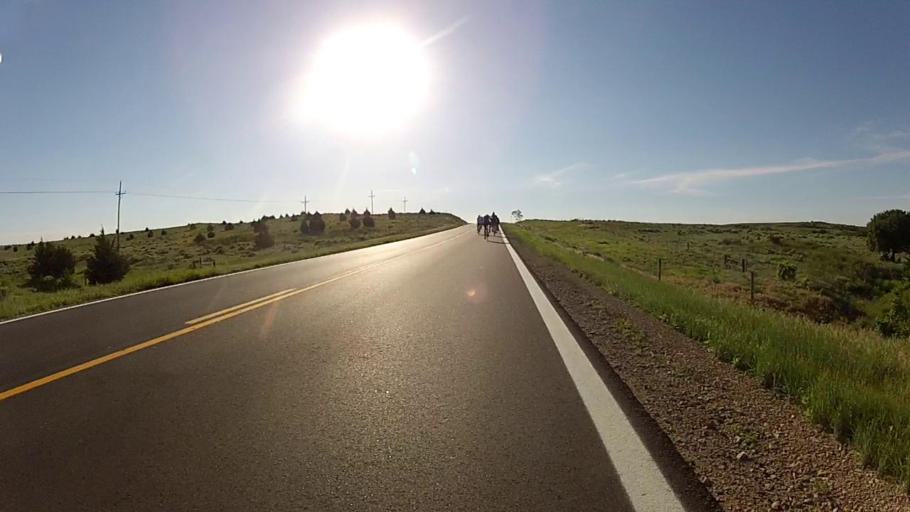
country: US
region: Kansas
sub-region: Comanche County
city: Coldwater
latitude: 37.2810
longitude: -99.0389
